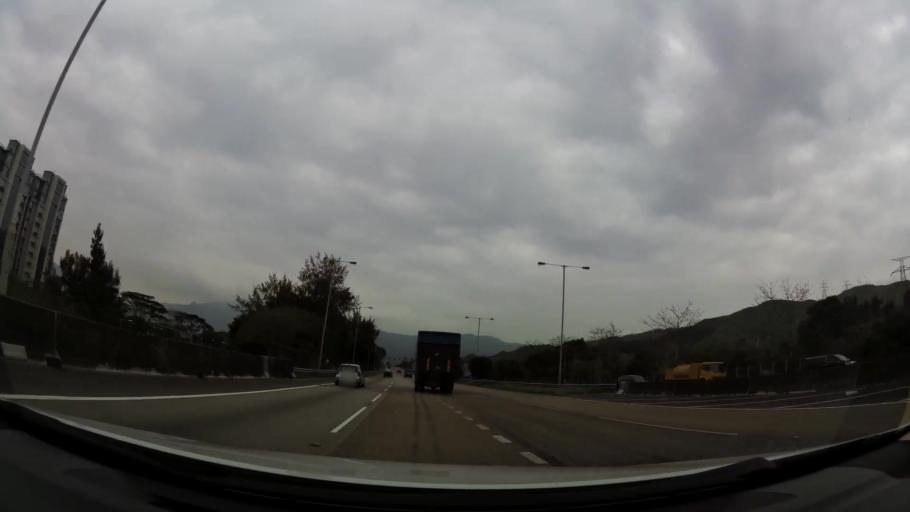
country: HK
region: Yuen Long
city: Yuen Long Kau Hui
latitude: 22.4417
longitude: 114.0528
